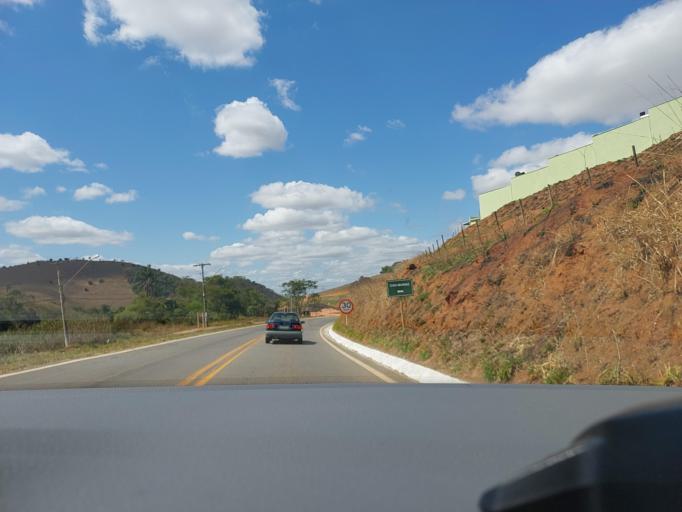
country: BR
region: Minas Gerais
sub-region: Muriae
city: Muriae
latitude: -21.1120
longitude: -42.4446
